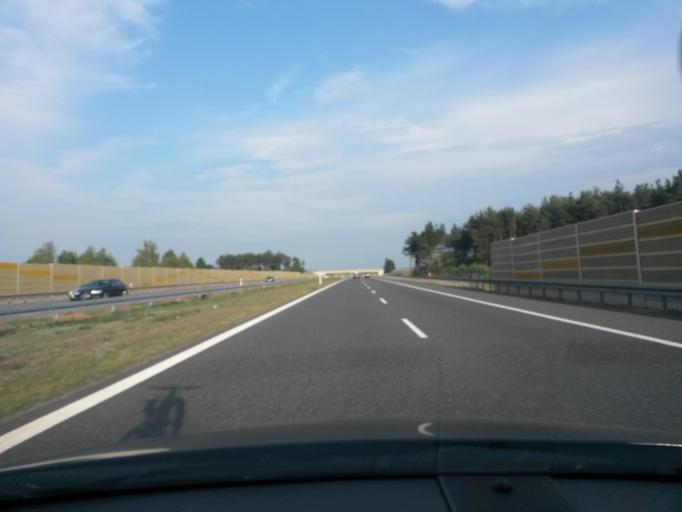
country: PL
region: Lodz Voivodeship
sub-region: Powiat zgierski
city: Ozorkow
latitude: 51.9341
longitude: 19.2717
